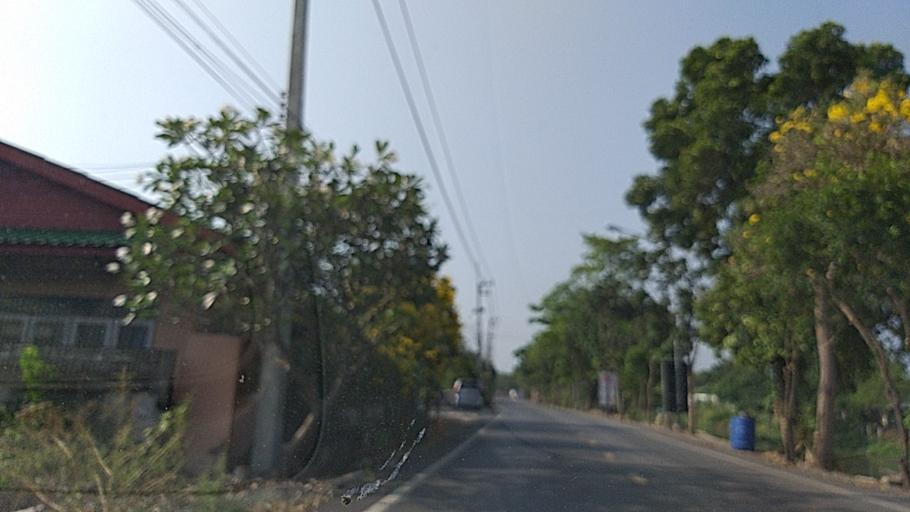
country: TH
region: Pathum Thani
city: Thanyaburi
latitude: 13.9910
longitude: 100.7060
